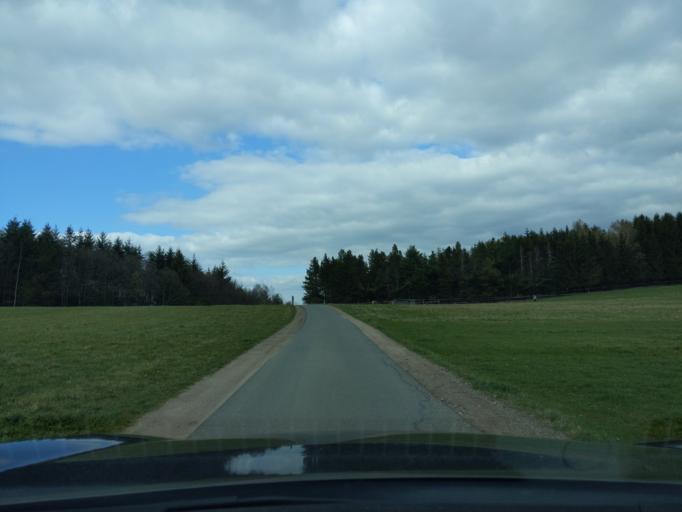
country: DE
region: Saxony
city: Schlema
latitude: 50.5920
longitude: 12.6684
